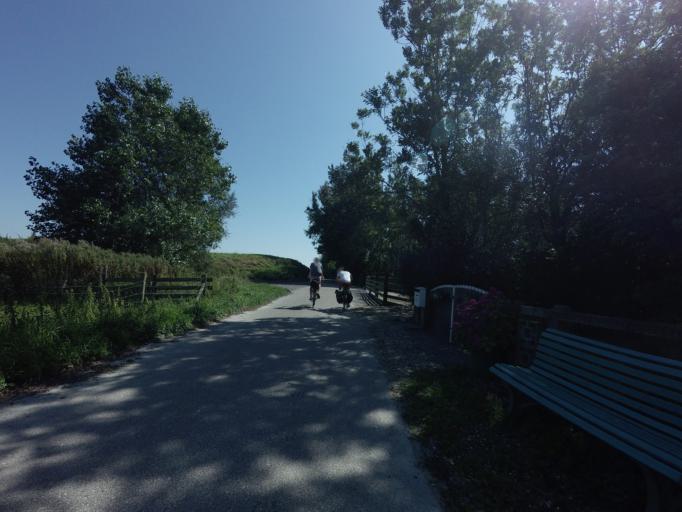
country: NL
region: Friesland
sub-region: Gemeente Dongeradeel
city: Anjum
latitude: 53.3972
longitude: 6.1048
